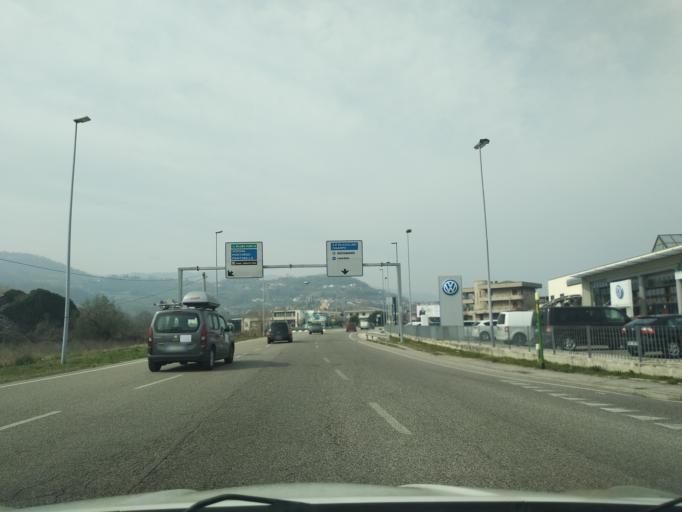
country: IT
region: Veneto
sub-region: Provincia di Vicenza
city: Arzignano
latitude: 45.5116
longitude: 11.3490
